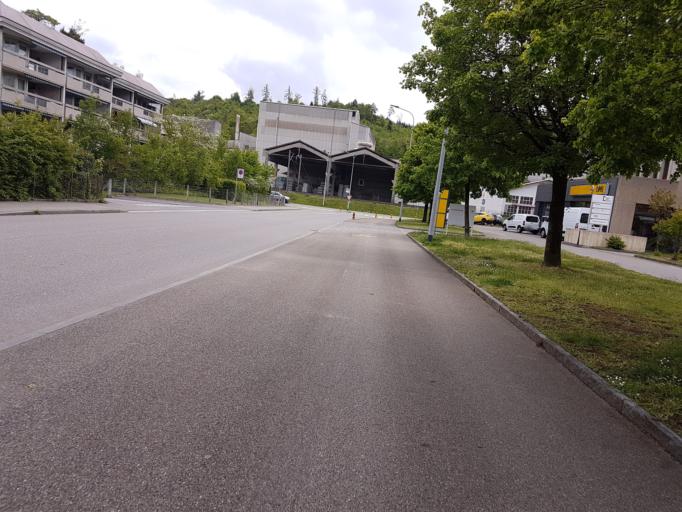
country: CH
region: Aargau
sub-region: Bezirk Brugg
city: Brugg
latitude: 47.4739
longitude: 8.1959
